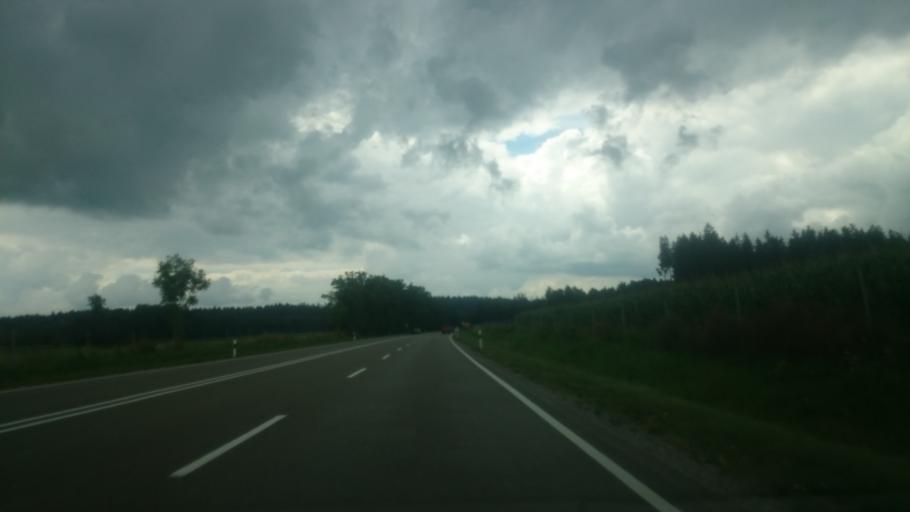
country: DE
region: Bavaria
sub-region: Swabia
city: Mauerstetten
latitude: 47.9157
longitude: 10.6584
